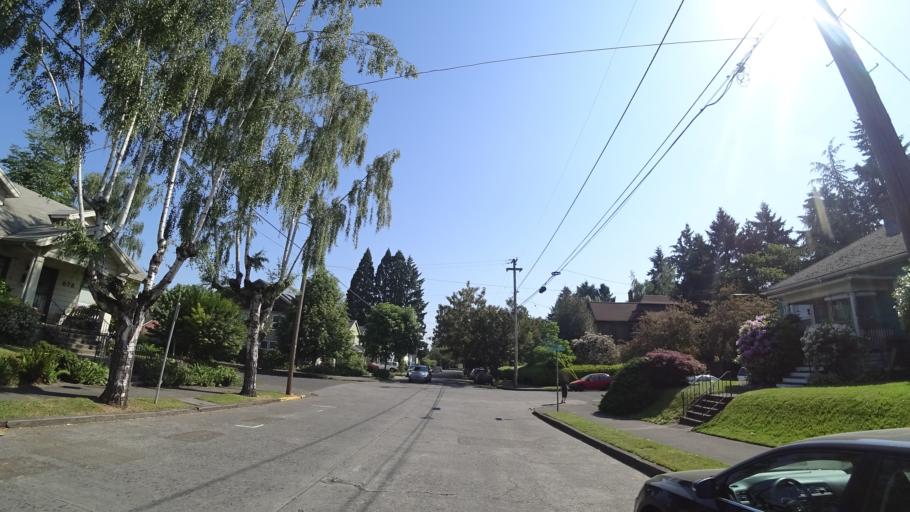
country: US
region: Oregon
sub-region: Multnomah County
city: Portland
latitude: 45.5725
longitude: -122.6558
